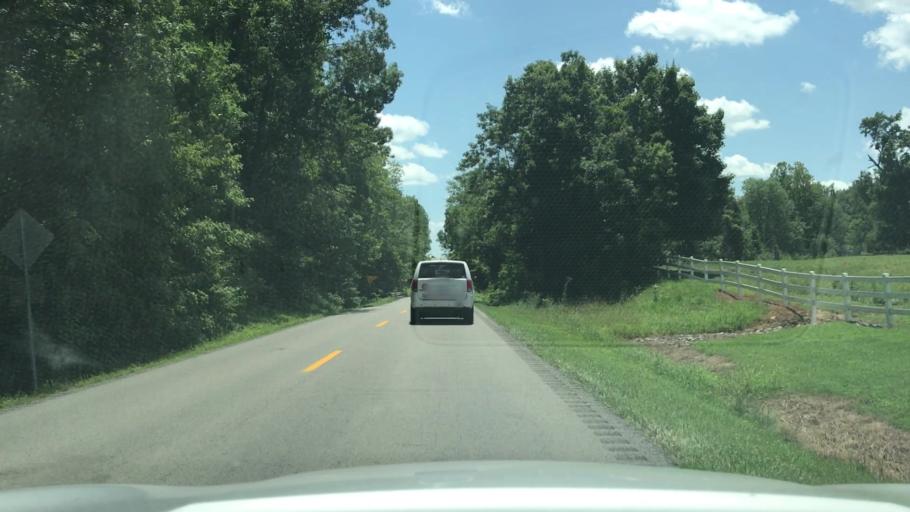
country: US
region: Kentucky
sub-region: Christian County
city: Hopkinsville
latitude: 36.9081
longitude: -87.4448
